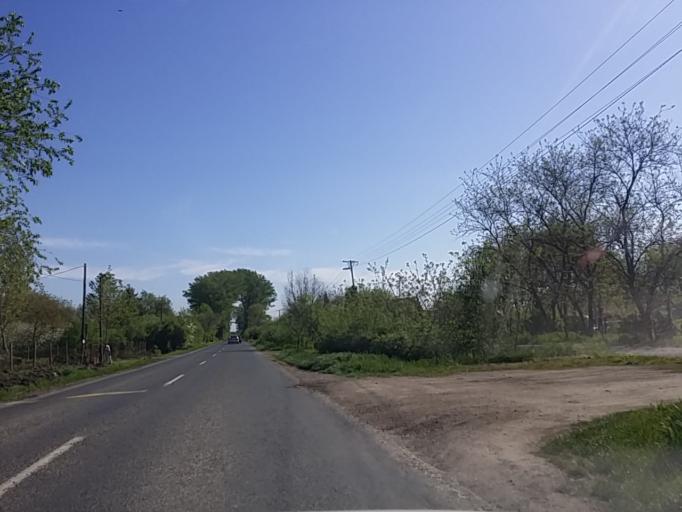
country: HU
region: Bekes
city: Bekes
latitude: 46.7098
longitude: 21.1774
